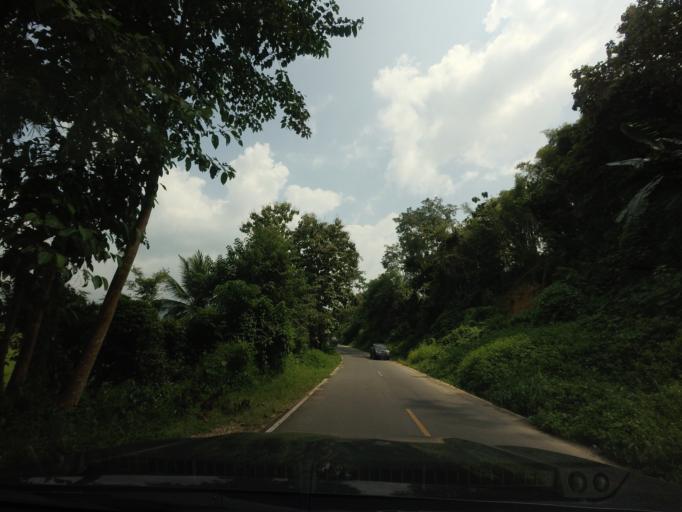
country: TH
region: Nan
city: Pua
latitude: 19.1679
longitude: 100.9301
